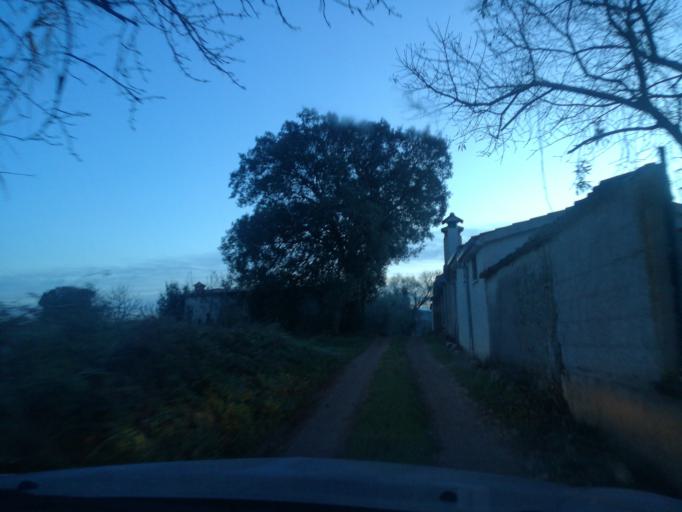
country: HR
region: Istarska
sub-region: Grad Rovinj
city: Rovinj
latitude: 45.1130
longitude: 13.6384
